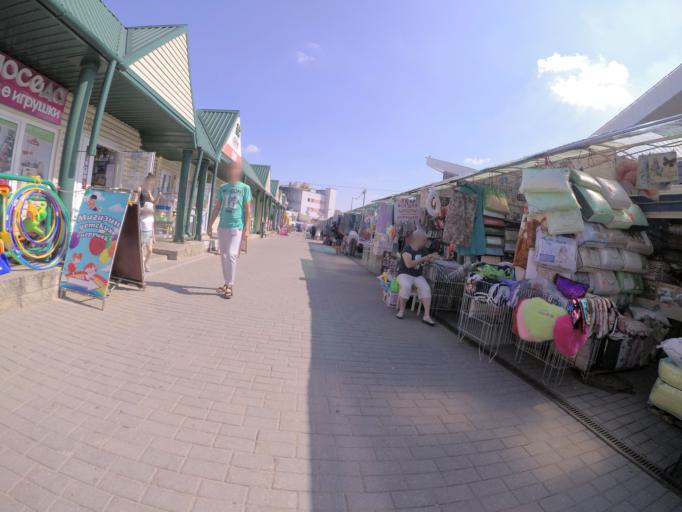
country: BY
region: Grodnenskaya
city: Hrodna
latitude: 53.6734
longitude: 23.8389
